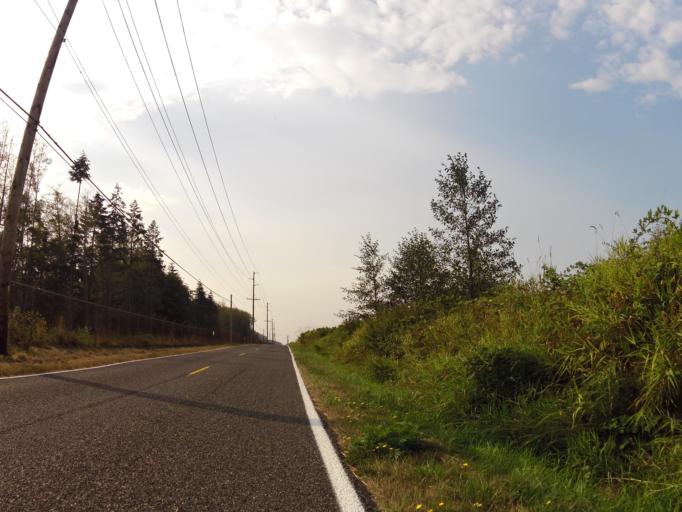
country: US
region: Washington
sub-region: Whatcom County
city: Birch Bay
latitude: 48.8818
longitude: -122.7489
